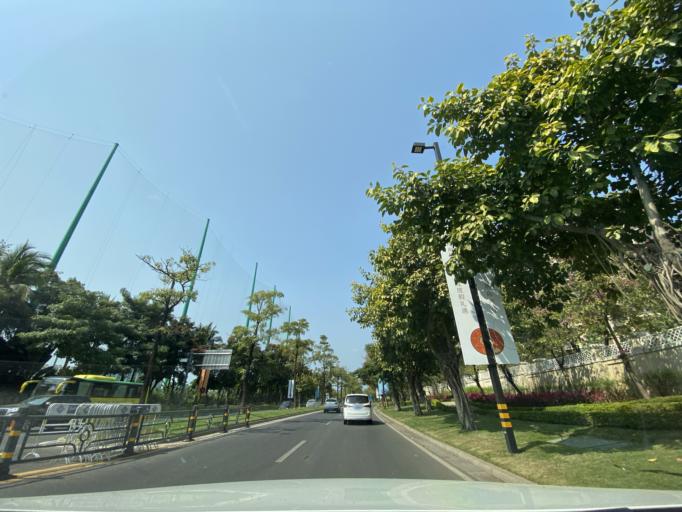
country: CN
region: Hainan
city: Yingzhou
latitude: 18.4025
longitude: 109.8498
